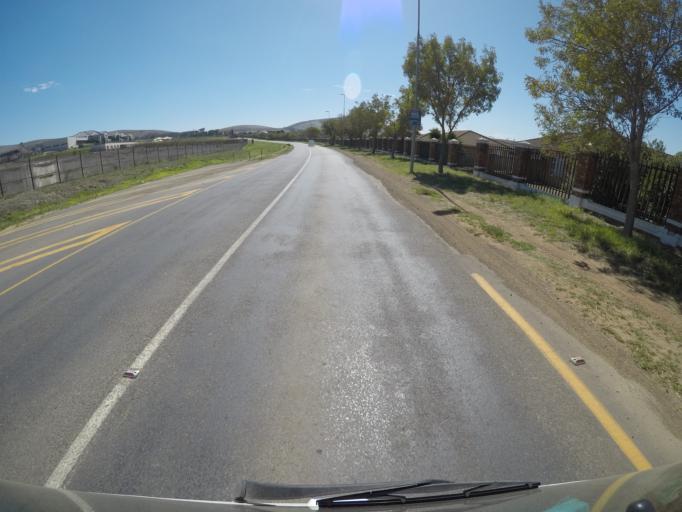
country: ZA
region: Western Cape
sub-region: City of Cape Town
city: Kraaifontein
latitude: -33.8167
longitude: 18.6340
